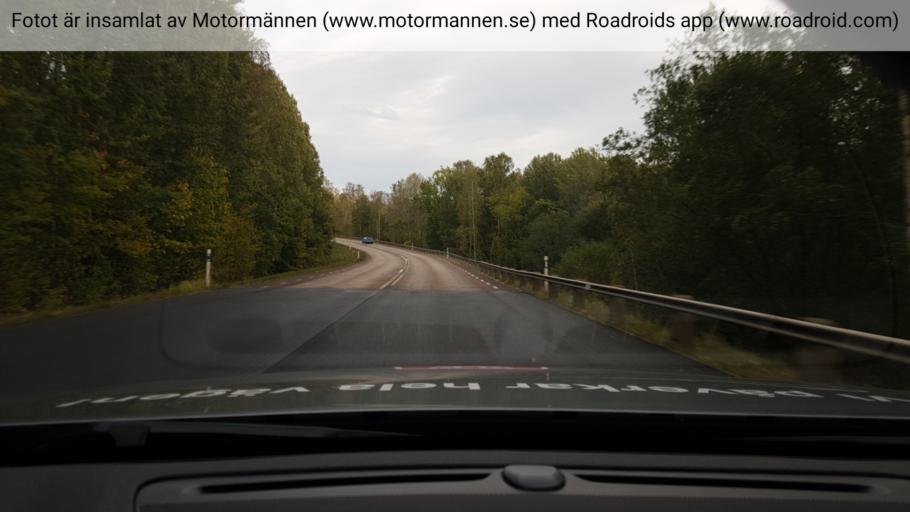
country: SE
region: Vaestra Goetaland
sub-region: Bengtsfors Kommun
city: Dals Langed
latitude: 59.0519
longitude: 12.4721
